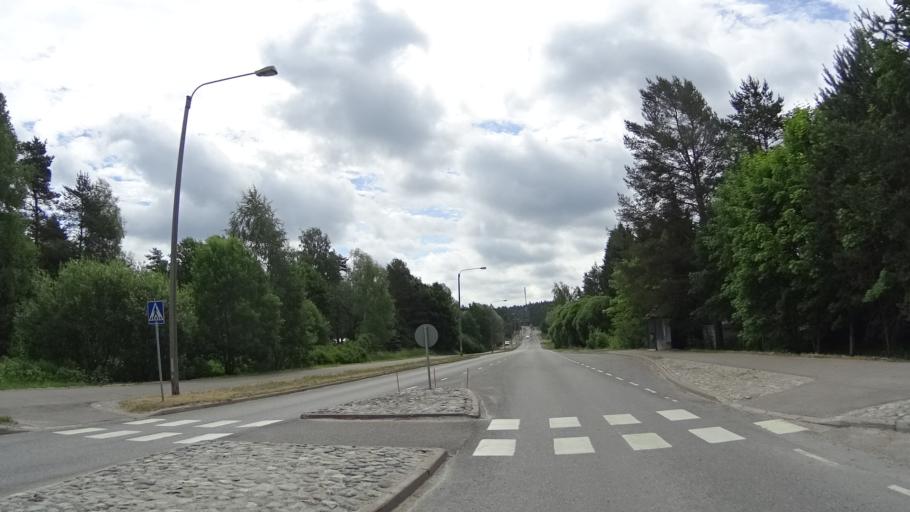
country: FI
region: Uusimaa
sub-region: Helsinki
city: Kirkkonummi
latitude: 60.2773
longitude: 24.4155
